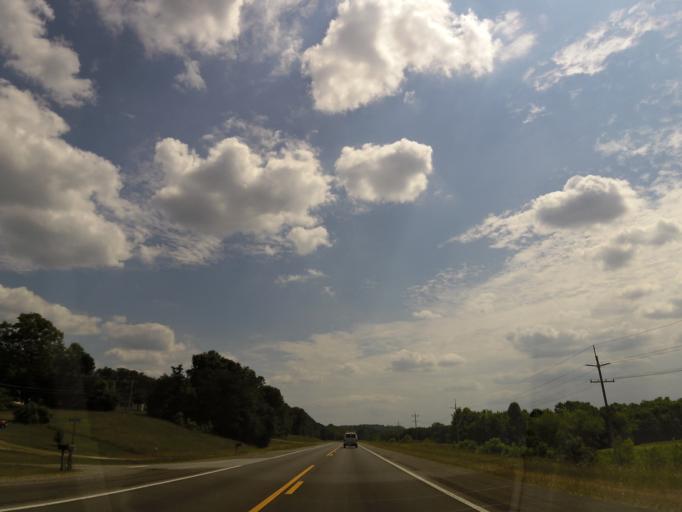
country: US
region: Tennessee
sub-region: Marion County
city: Jasper
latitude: 35.1161
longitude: -85.5691
